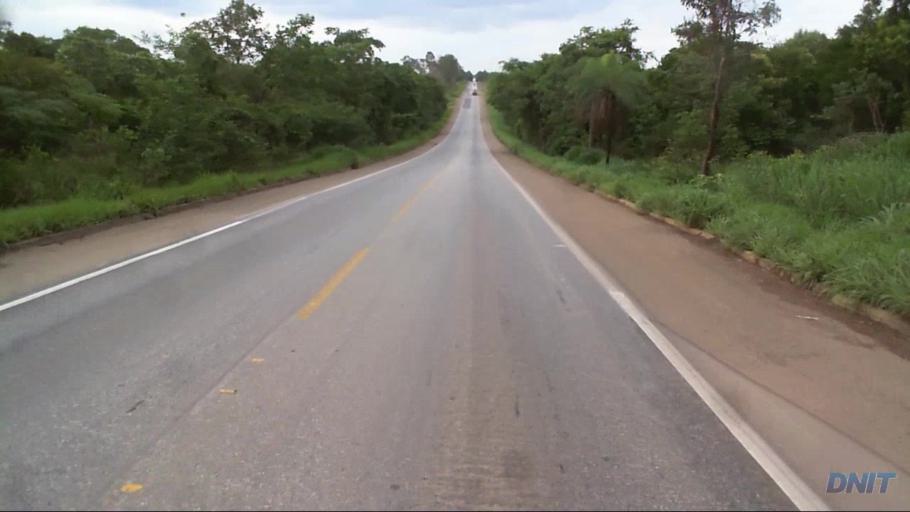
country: BR
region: Goias
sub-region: Uruacu
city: Uruacu
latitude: -14.6124
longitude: -49.1687
